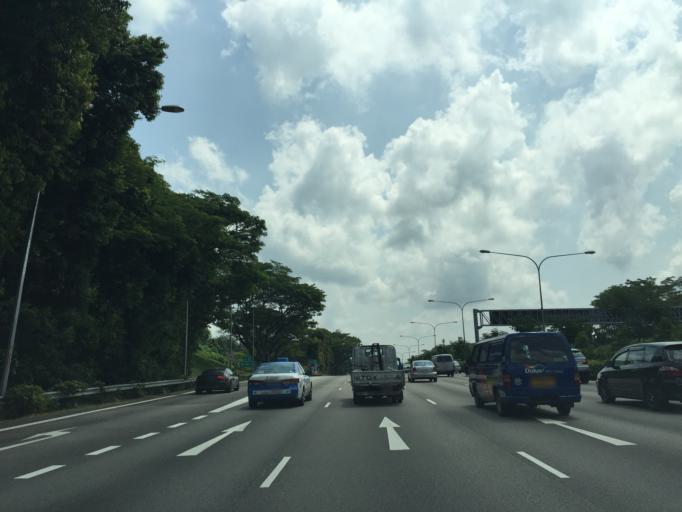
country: SG
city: Singapore
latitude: 1.3375
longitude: 103.8082
